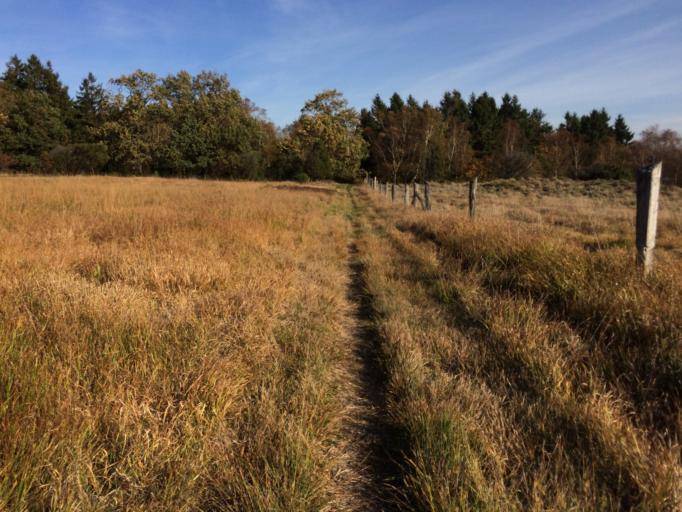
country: DK
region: Central Jutland
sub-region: Holstebro Kommune
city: Ulfborg
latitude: 56.2684
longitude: 8.4718
